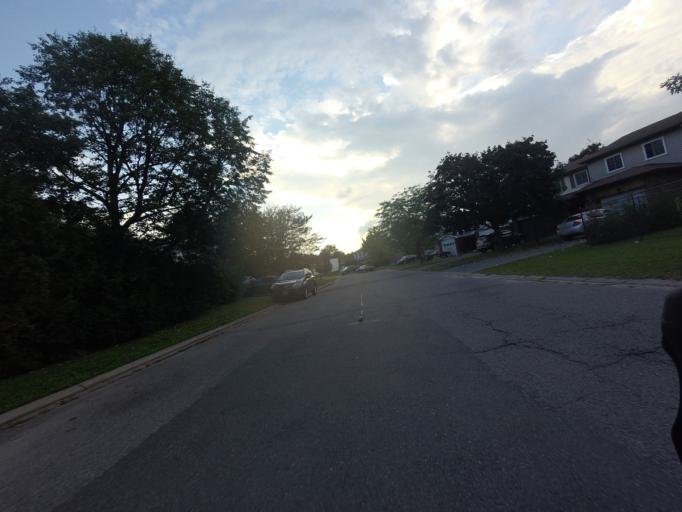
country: CA
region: Ontario
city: Bells Corners
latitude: 45.2744
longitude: -75.7532
